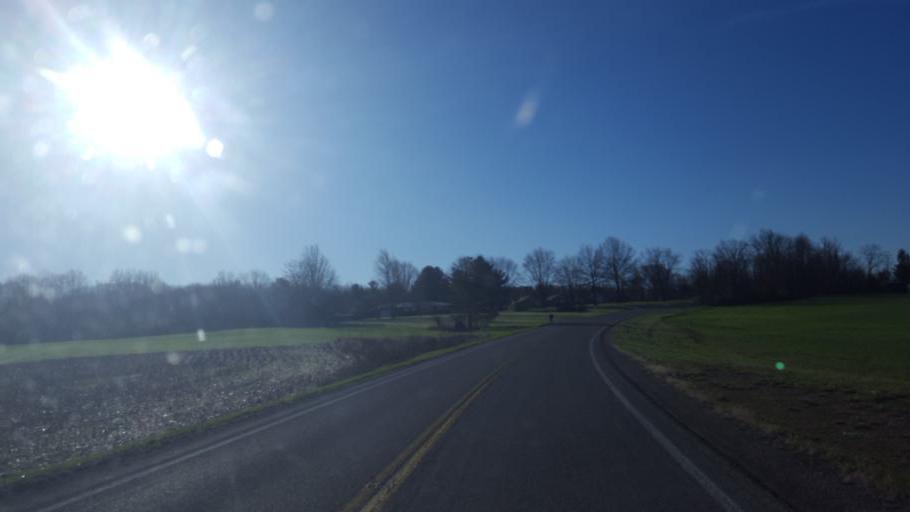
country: US
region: Ohio
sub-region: Morrow County
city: Mount Gilead
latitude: 40.5350
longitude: -82.8227
